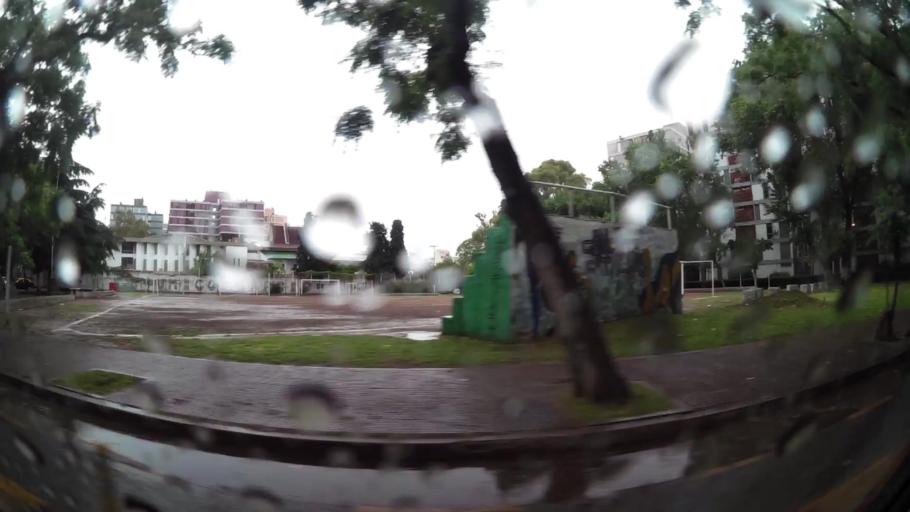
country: AR
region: Buenos Aires F.D.
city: Buenos Aires
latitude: -34.6267
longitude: -58.3646
